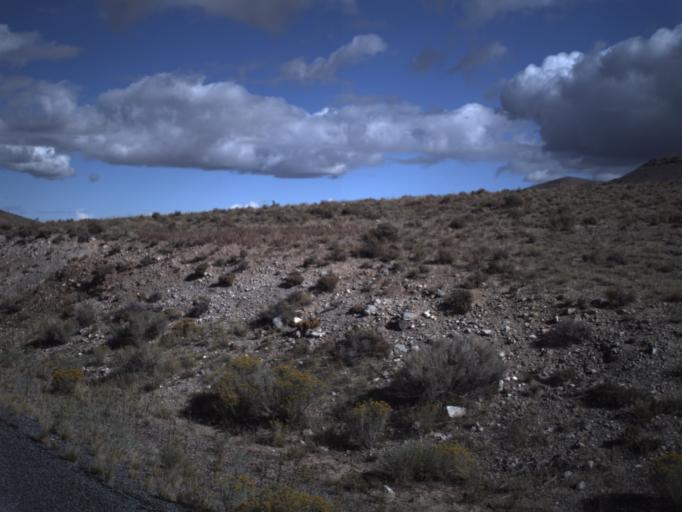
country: US
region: Utah
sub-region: Beaver County
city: Milford
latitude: 38.6219
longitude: -113.8478
